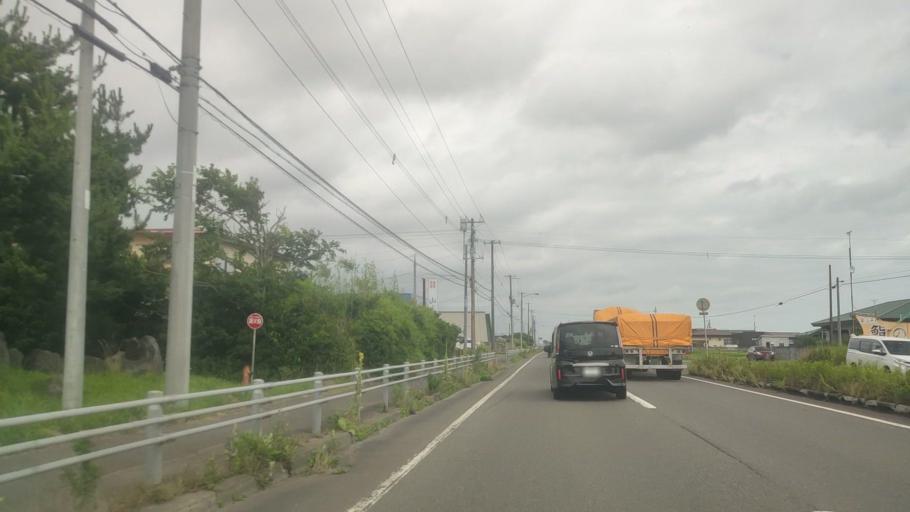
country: JP
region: Hokkaido
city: Shiraoi
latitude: 42.4733
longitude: 141.2347
